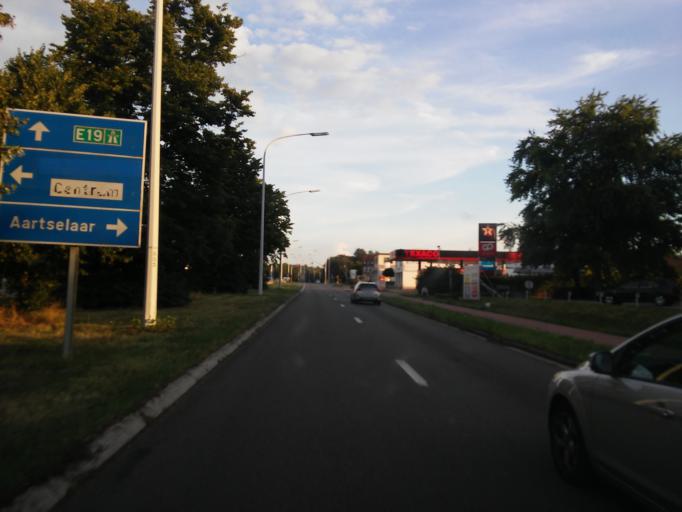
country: BE
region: Flanders
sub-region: Provincie Antwerpen
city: Kontich
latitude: 51.1397
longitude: 4.4382
